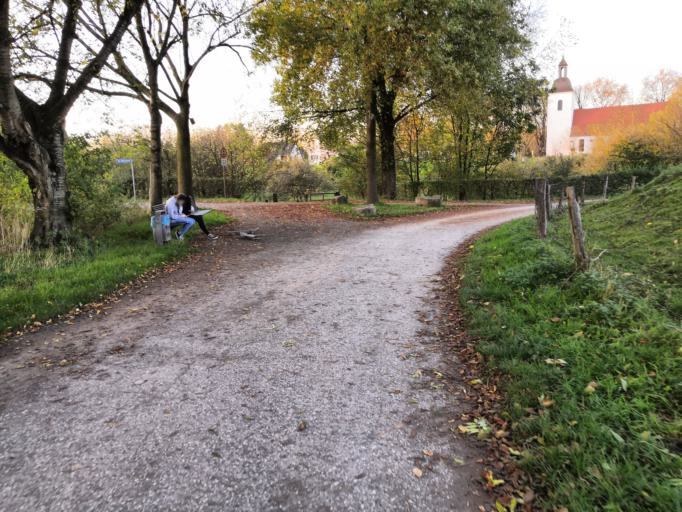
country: DE
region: North Rhine-Westphalia
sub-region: Regierungsbezirk Dusseldorf
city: Hochfeld
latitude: 51.3797
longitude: 6.7030
